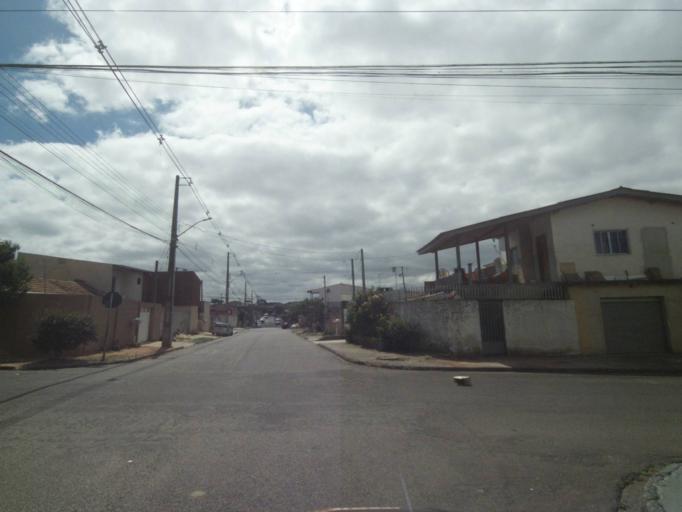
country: BR
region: Parana
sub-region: Sao Jose Dos Pinhais
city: Sao Jose dos Pinhais
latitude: -25.5563
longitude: -49.2642
